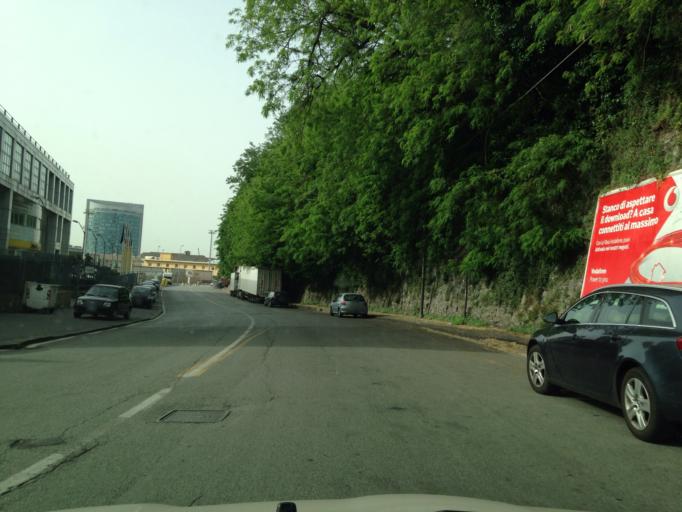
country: IT
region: Liguria
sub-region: Provincia di Genova
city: San Teodoro
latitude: 44.4209
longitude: 8.8783
